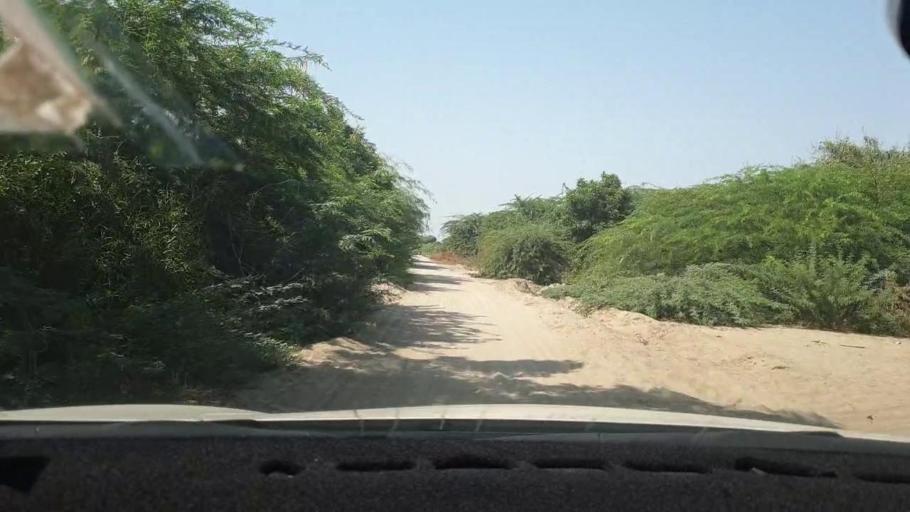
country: PK
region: Sindh
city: Tando Mittha Khan
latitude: 25.8627
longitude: 69.3853
